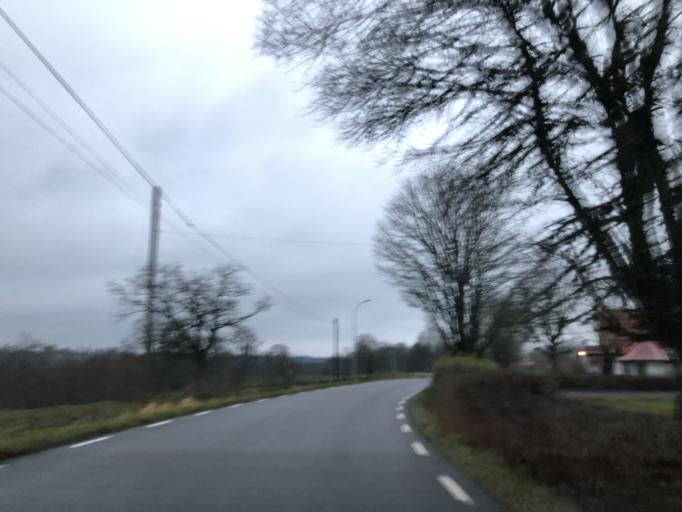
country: SE
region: Vaestra Goetaland
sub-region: Boras Kommun
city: Dalsjofors
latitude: 57.8387
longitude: 13.2240
